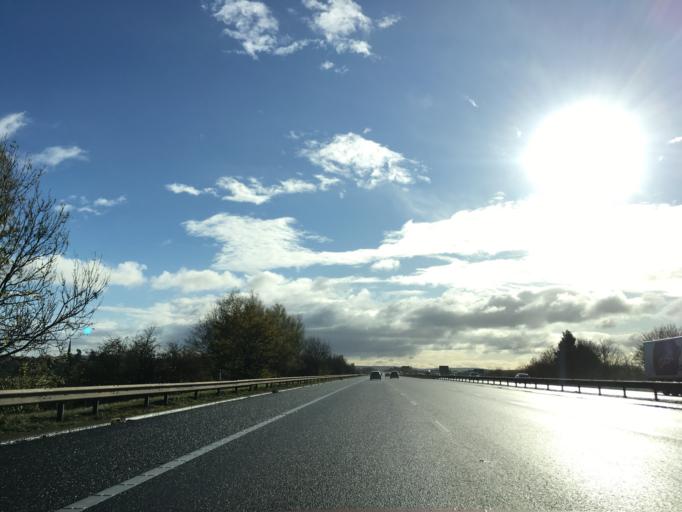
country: GB
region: England
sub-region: Worcestershire
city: Bredon
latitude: 52.0378
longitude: -2.1294
